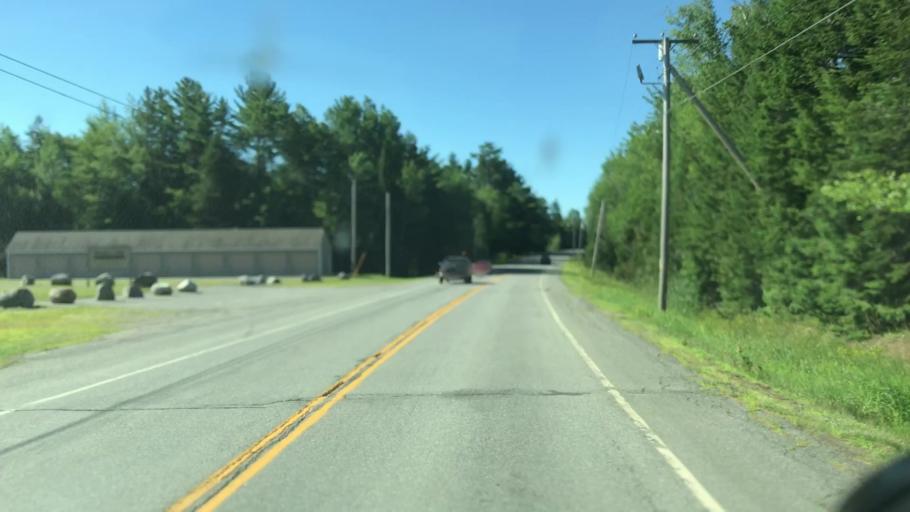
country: US
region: Maine
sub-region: Penobscot County
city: Howland
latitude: 45.2545
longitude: -68.6376
